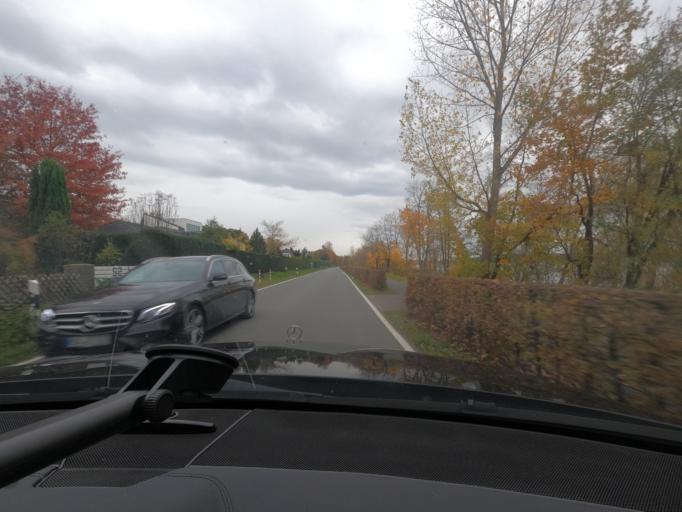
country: DE
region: North Rhine-Westphalia
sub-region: Regierungsbezirk Arnsberg
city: Mohnesee
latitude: 51.4861
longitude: 8.1428
